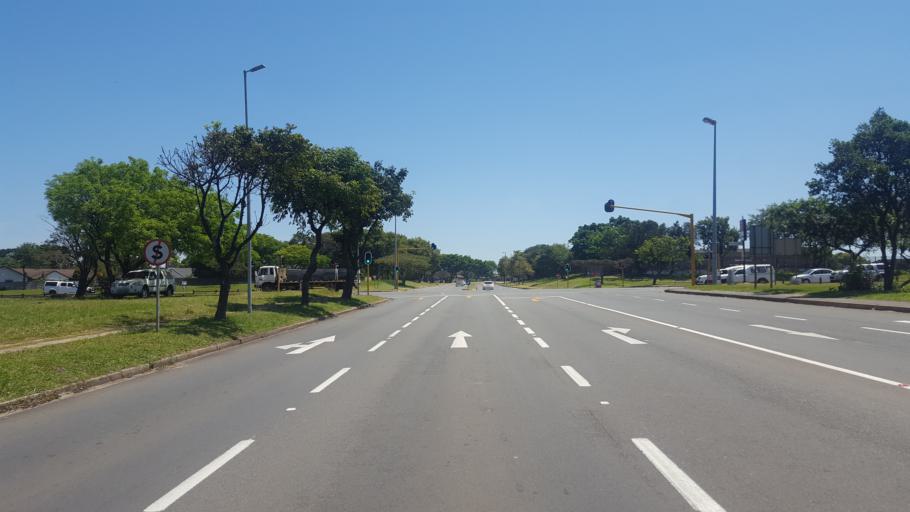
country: ZA
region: KwaZulu-Natal
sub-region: uThungulu District Municipality
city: Richards Bay
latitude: -28.7614
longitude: 32.0598
